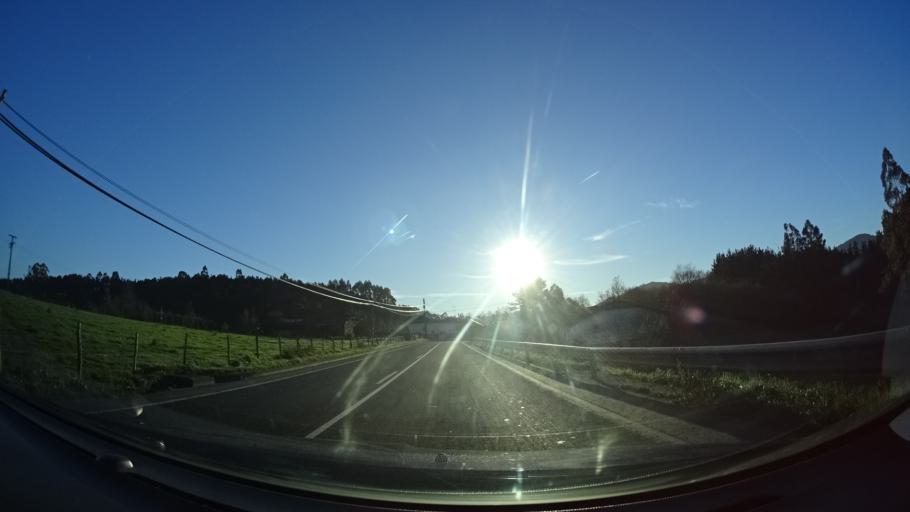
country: ES
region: Basque Country
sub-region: Bizkaia
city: Kortezubi
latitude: 43.3307
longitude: -2.6593
